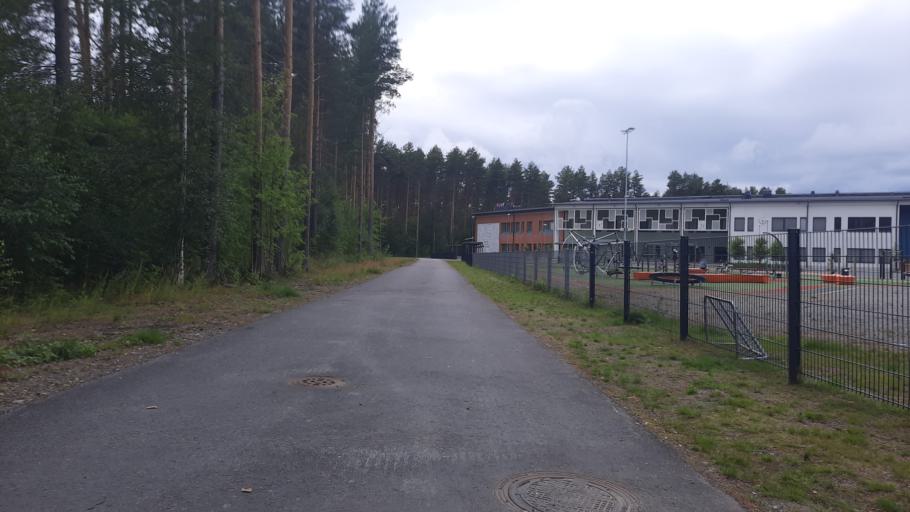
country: FI
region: North Karelia
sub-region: Joensuu
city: Joensuu
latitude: 62.6124
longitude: 29.8227
